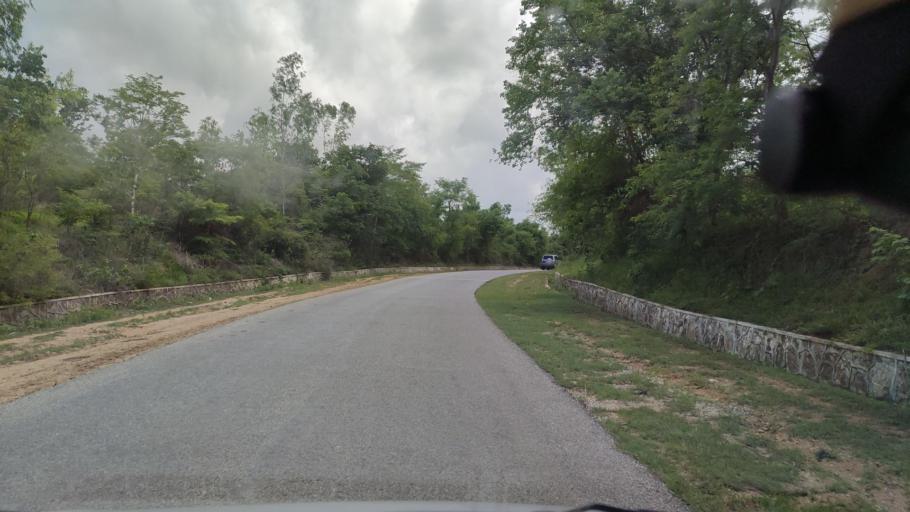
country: MM
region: Magway
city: Taungdwingyi
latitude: 20.1476
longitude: 95.6256
